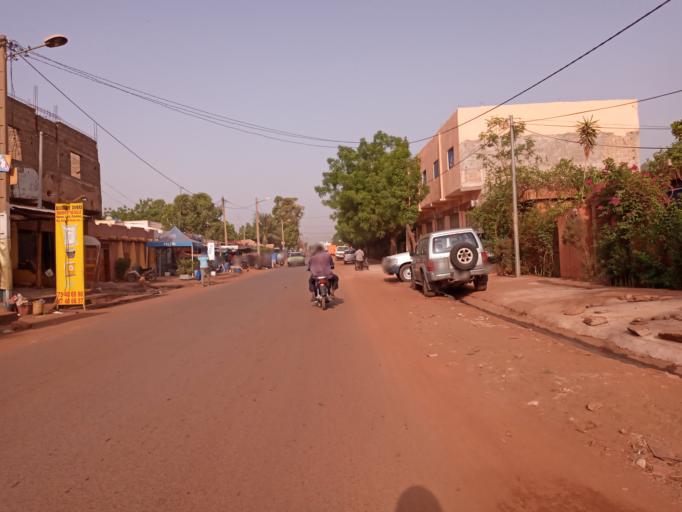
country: ML
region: Bamako
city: Bamako
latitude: 12.6643
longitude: -7.9763
